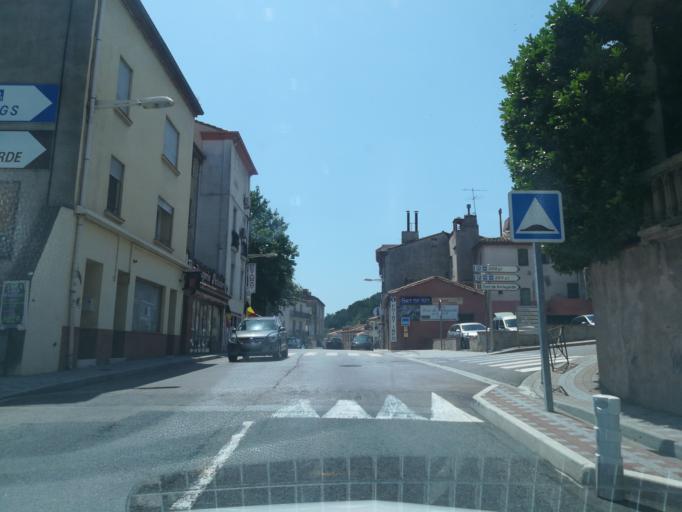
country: ES
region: Catalonia
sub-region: Provincia de Girona
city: la Jonquera
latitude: 42.4654
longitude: 2.8632
